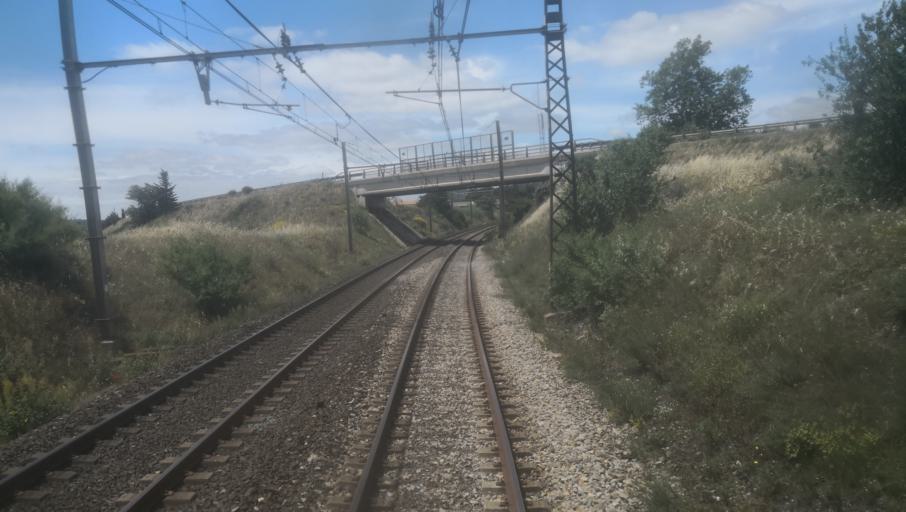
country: FR
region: Languedoc-Roussillon
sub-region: Departement de l'Aude
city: Moussan
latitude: 43.1825
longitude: 2.9457
